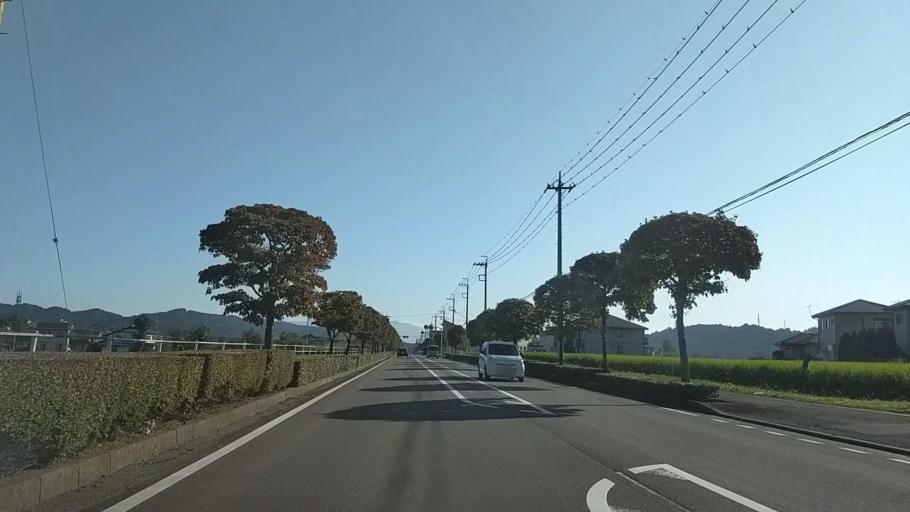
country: JP
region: Gunma
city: Annaka
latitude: 36.3204
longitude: 138.8917
